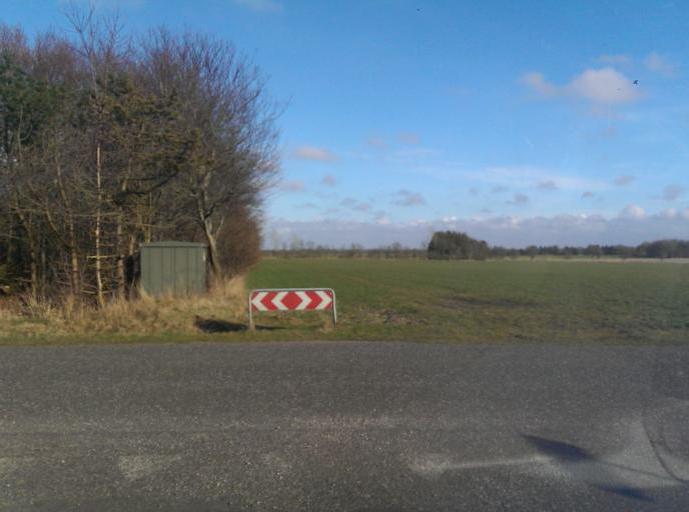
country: DK
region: South Denmark
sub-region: Esbjerg Kommune
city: Bramming
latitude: 55.4517
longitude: 8.7523
